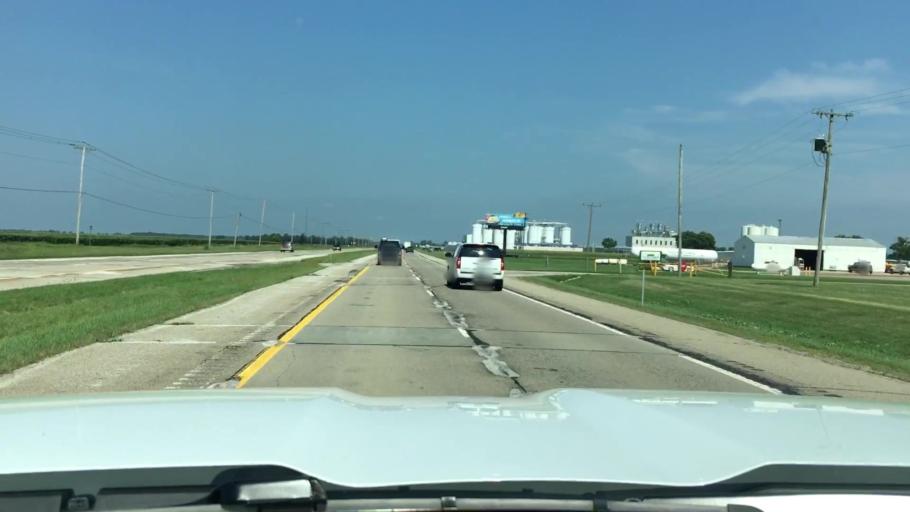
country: US
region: Michigan
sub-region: Kalamazoo County
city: Schoolcraft
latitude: 42.0731
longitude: -85.6364
